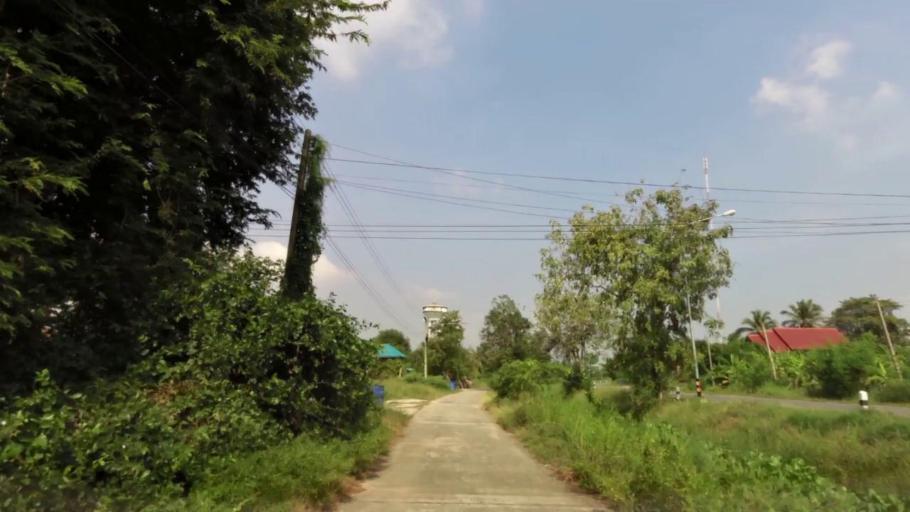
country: TH
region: Ang Thong
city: Wiset Chaichan
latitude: 14.6054
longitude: 100.3956
